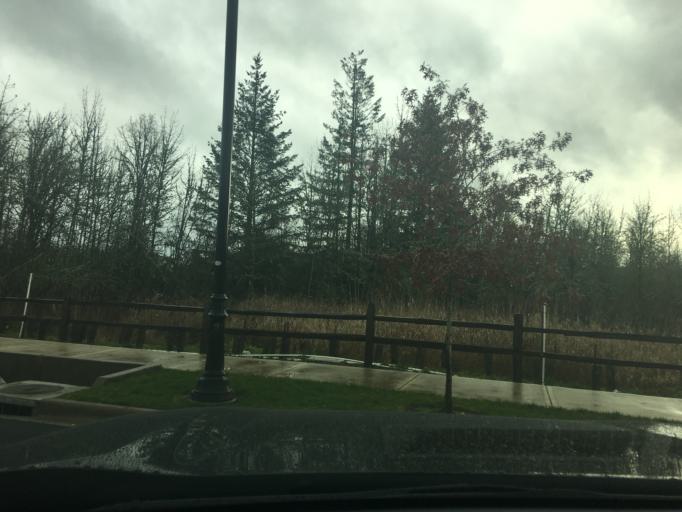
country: US
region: Oregon
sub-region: Washington County
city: Bethany
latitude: 45.5720
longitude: -122.8476
